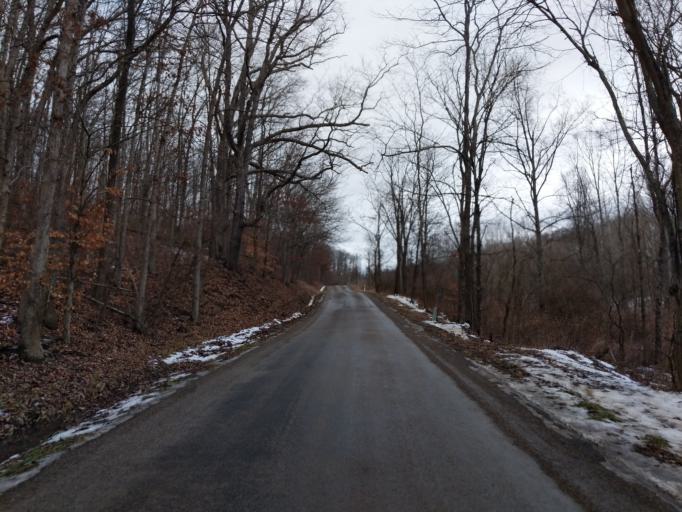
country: US
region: Ohio
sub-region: Athens County
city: The Plains
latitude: 39.3373
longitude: -82.1542
